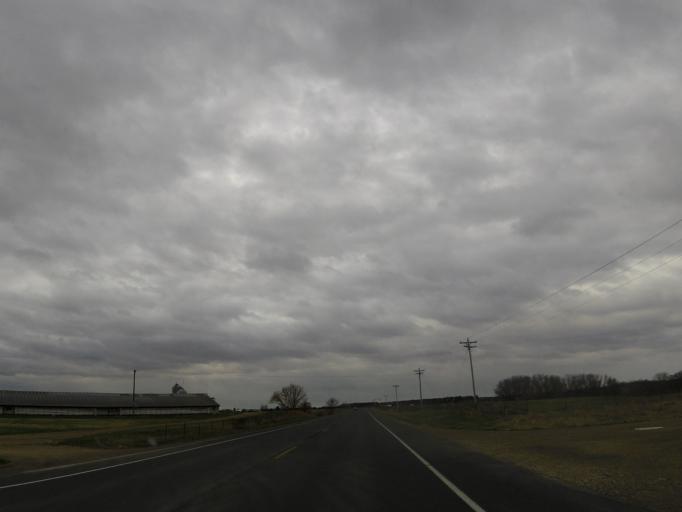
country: US
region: Wisconsin
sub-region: Saint Croix County
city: New Richmond
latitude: 45.0971
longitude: -92.5627
